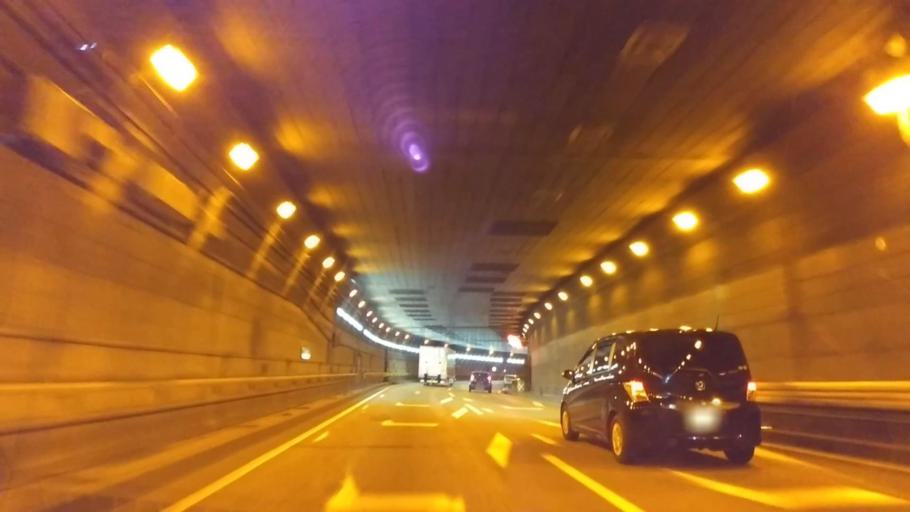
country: JP
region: Kanagawa
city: Minami-rinkan
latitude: 35.4892
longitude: 139.4624
